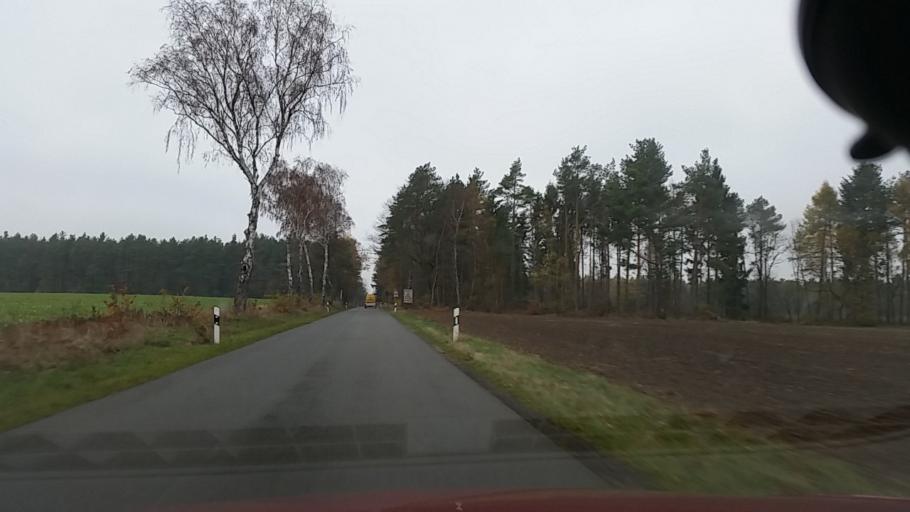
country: DE
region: Lower Saxony
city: Obernholz
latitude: 52.7789
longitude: 10.5816
